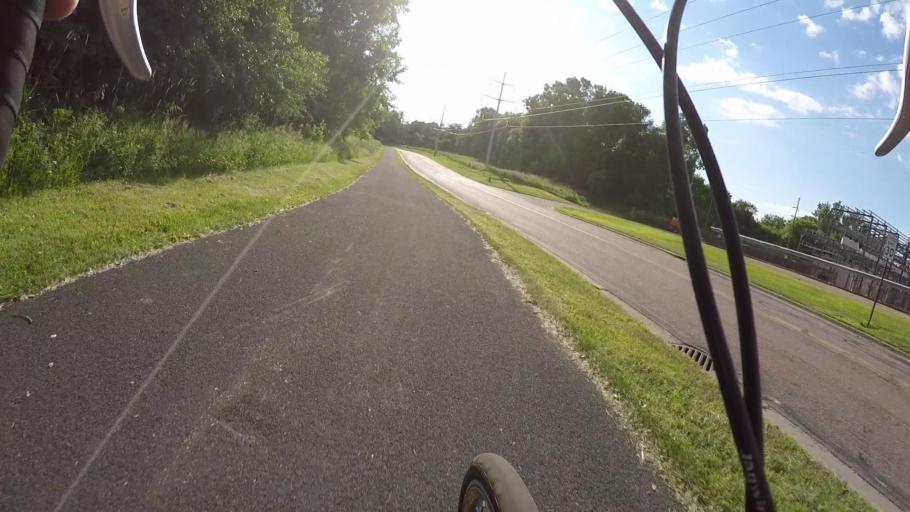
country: US
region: Minnesota
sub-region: Hennepin County
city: Eden Prairie
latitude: 44.8633
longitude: -93.4700
